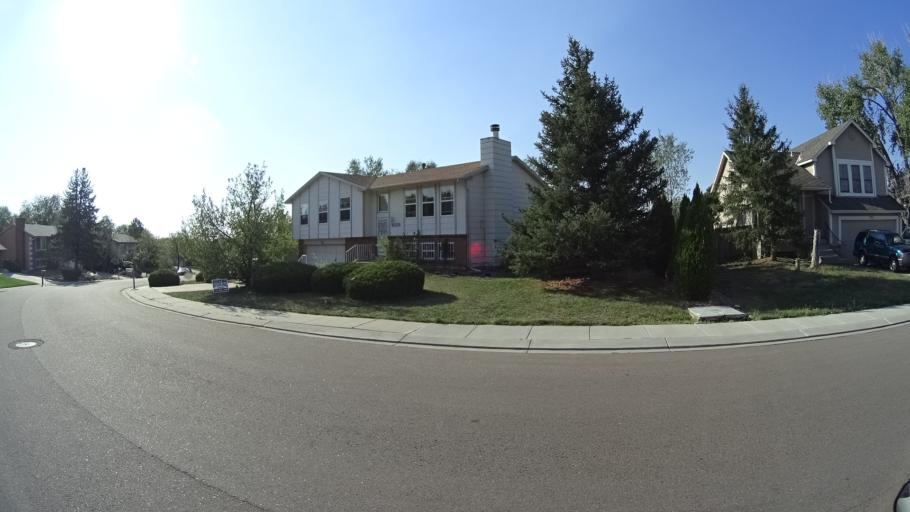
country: US
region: Colorado
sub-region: El Paso County
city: Stratmoor
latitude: 38.7797
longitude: -104.8096
